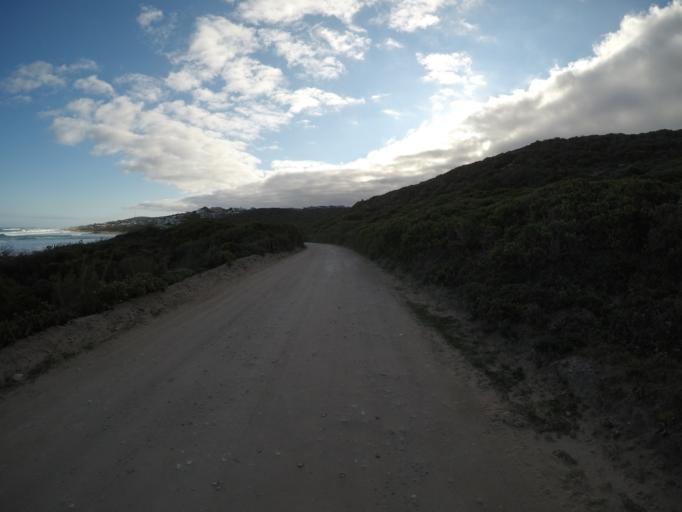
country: ZA
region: Western Cape
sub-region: Eden District Municipality
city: Riversdale
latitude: -34.4187
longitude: 21.3546
